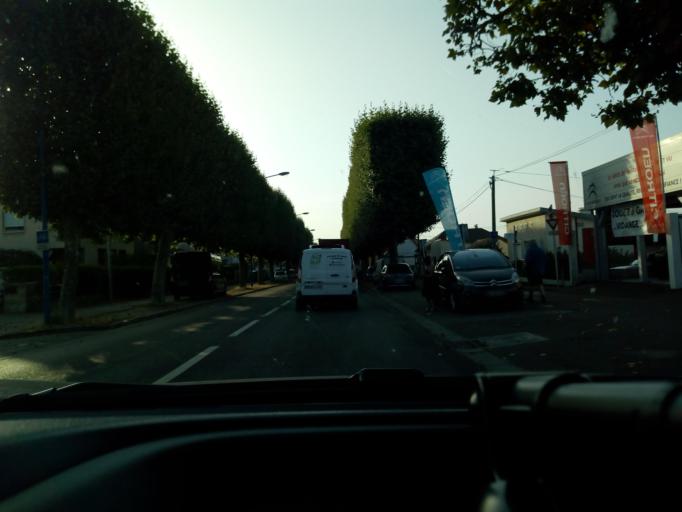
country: FR
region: Haute-Normandie
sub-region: Departement de la Seine-Maritime
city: Sotteville-les-Rouen
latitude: 49.4092
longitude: 1.0847
